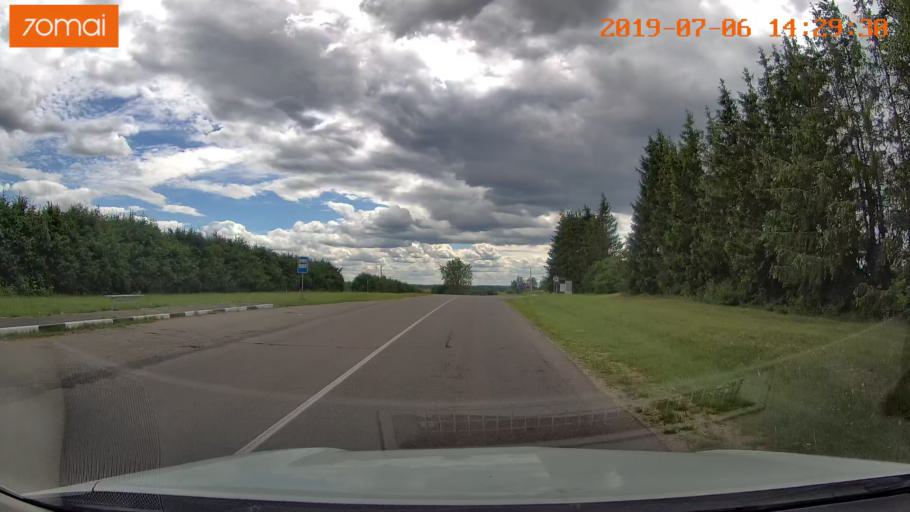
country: BY
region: Minsk
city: Ivyanyets
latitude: 53.9336
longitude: 26.7959
